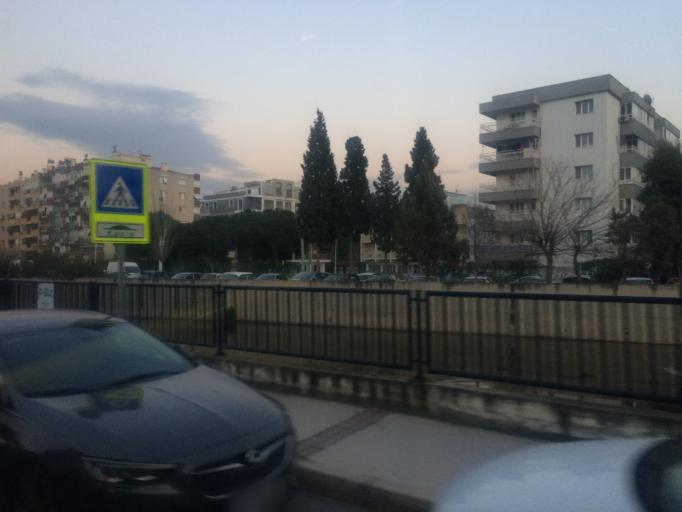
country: TR
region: Izmir
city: Karsiyaka
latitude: 38.4613
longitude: 27.0960
